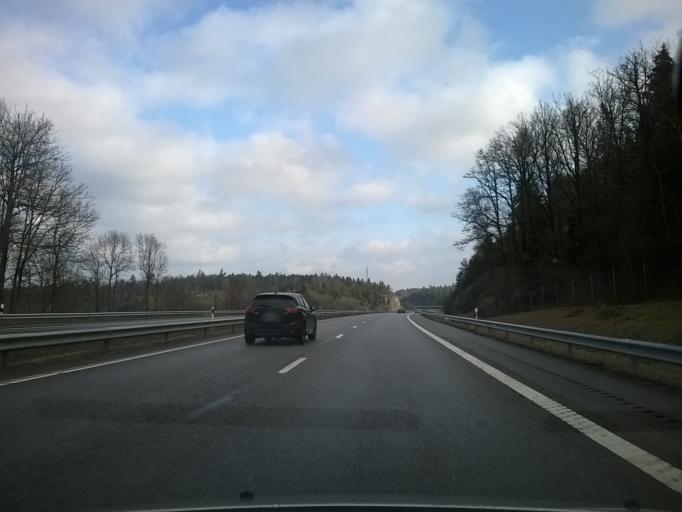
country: SE
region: Vaestra Goetaland
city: Svanesund
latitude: 58.1476
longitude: 11.8845
